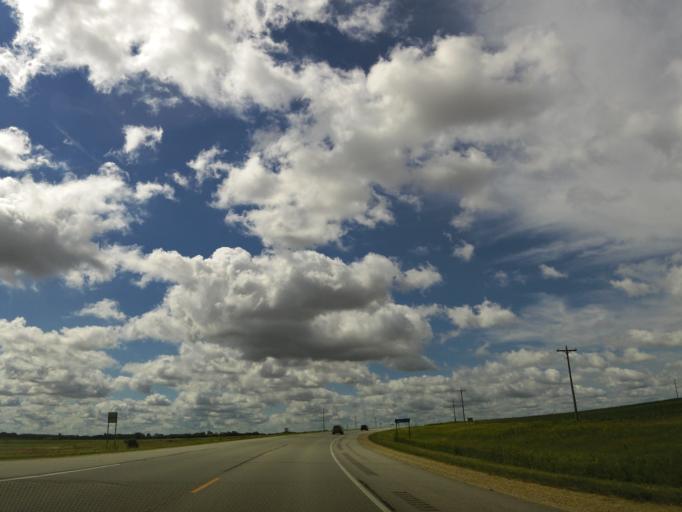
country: US
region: Minnesota
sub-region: Olmsted County
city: Stewartville
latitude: 43.7634
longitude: -92.4794
